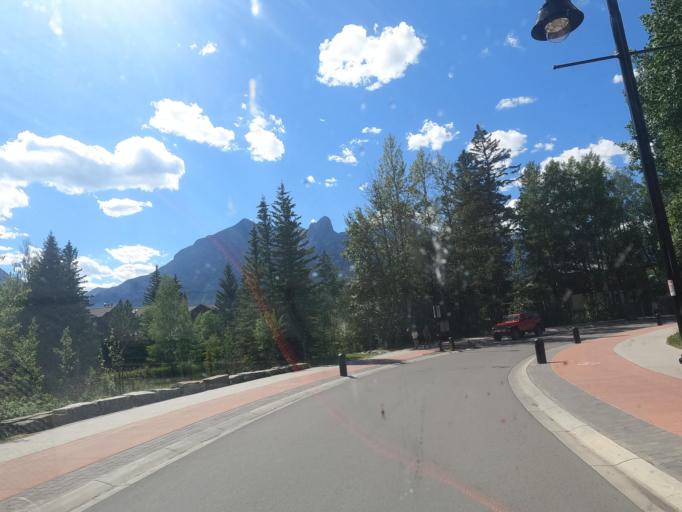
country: CA
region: Alberta
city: Canmore
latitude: 51.0883
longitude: -115.3554
